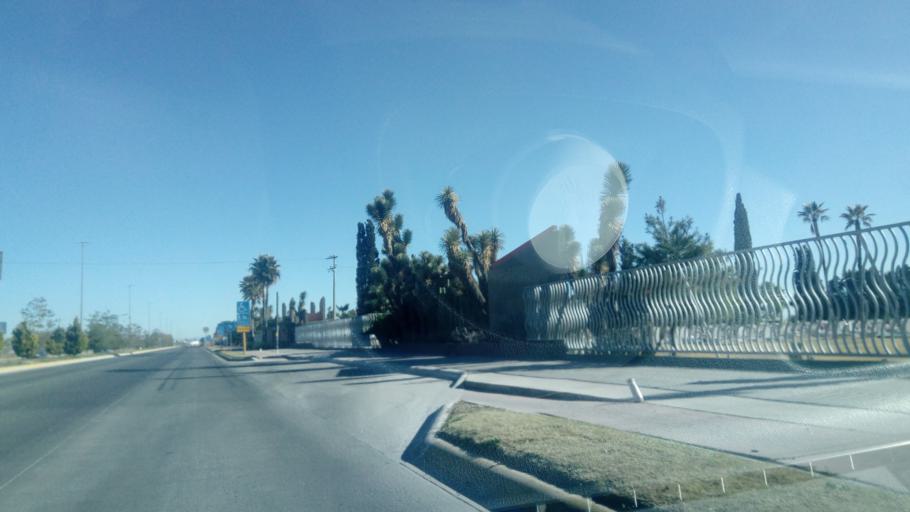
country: MX
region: Durango
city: Victoria de Durango
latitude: 24.0813
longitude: -104.5870
